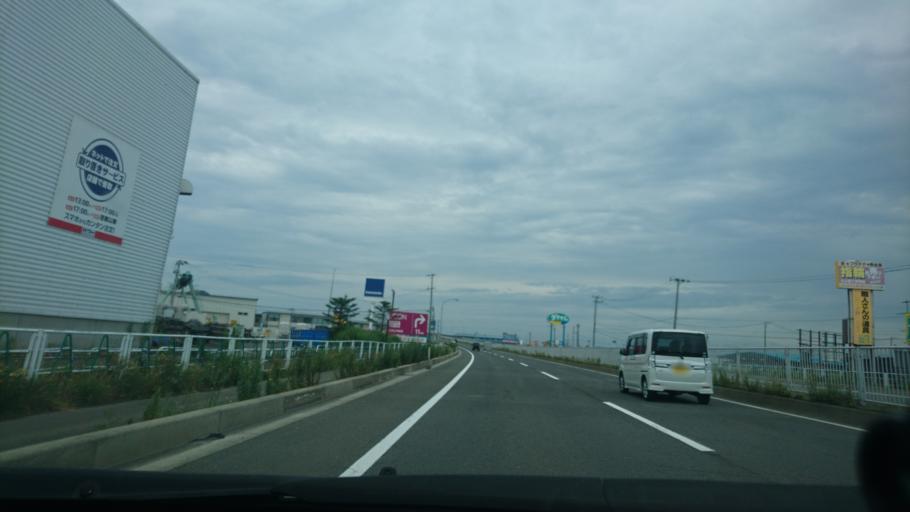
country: JP
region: Akita
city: Omagari
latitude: 39.4719
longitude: 140.4837
